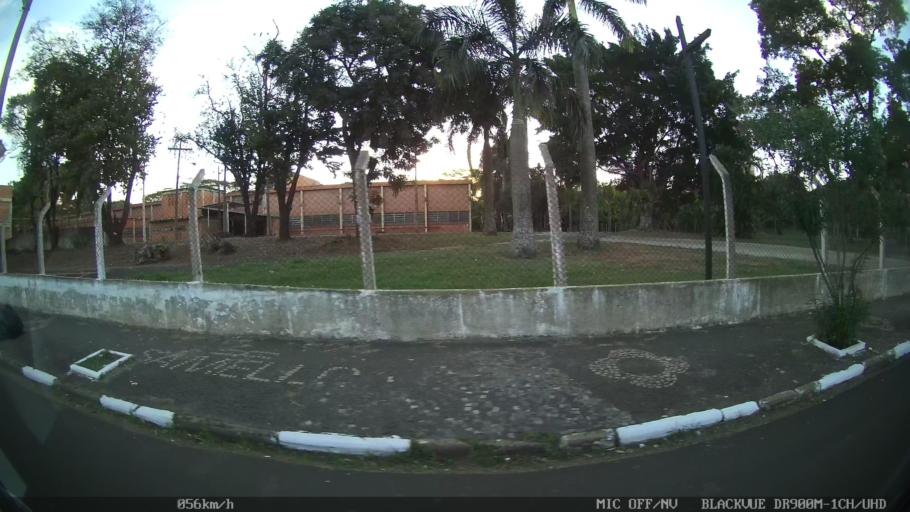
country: BR
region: Sao Paulo
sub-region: Franca
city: Franca
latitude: -20.5316
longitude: -47.4046
